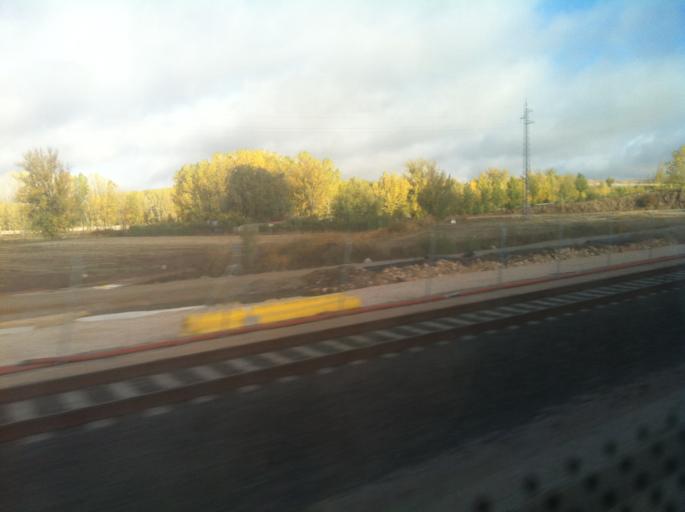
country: ES
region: Castille and Leon
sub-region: Provincia de Burgos
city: San Mames de Burgos
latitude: 42.3349
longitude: -3.8017
